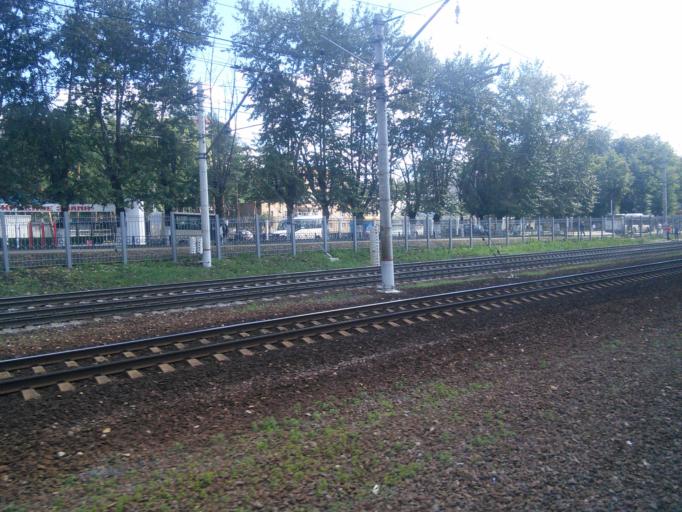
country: RU
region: Moskovskaya
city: Ramenskoye
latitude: 55.5741
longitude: 38.2036
